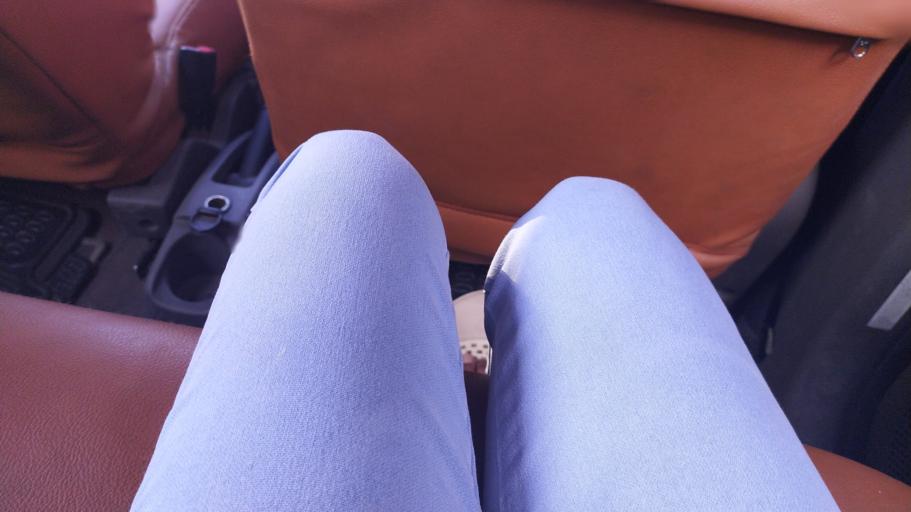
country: IN
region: Telangana
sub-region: Rangareddi
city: Balapur
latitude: 17.3152
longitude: 78.4425
